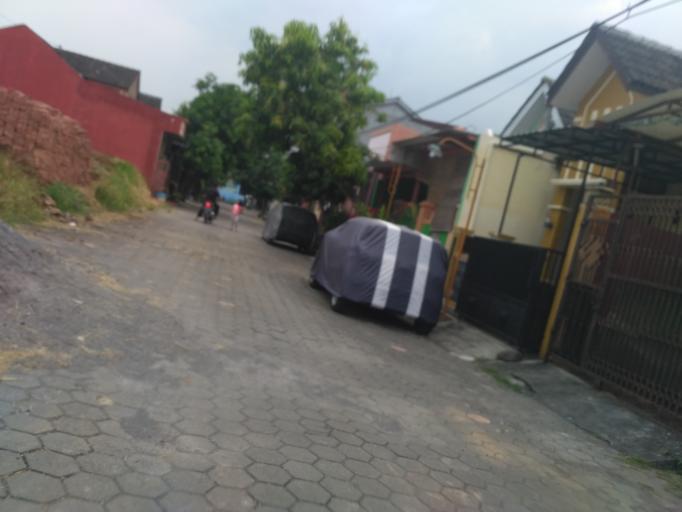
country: ID
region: Central Java
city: Mranggen
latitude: -7.0405
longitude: 110.4701
